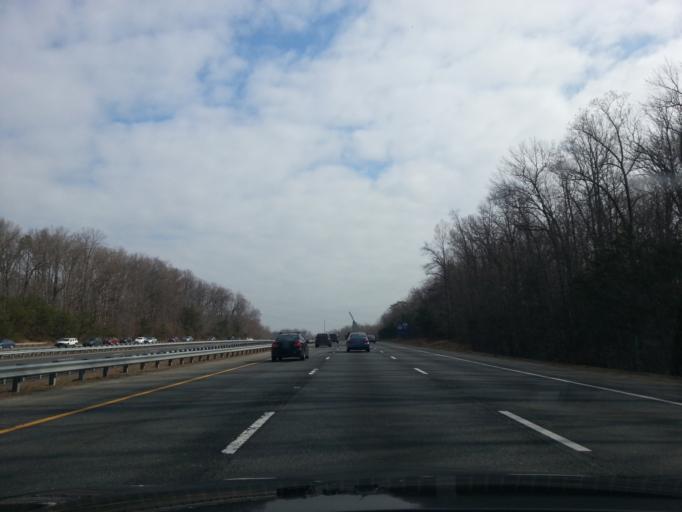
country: US
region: Virginia
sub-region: Prince William County
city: Triangle
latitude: 38.5369
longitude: -77.3522
